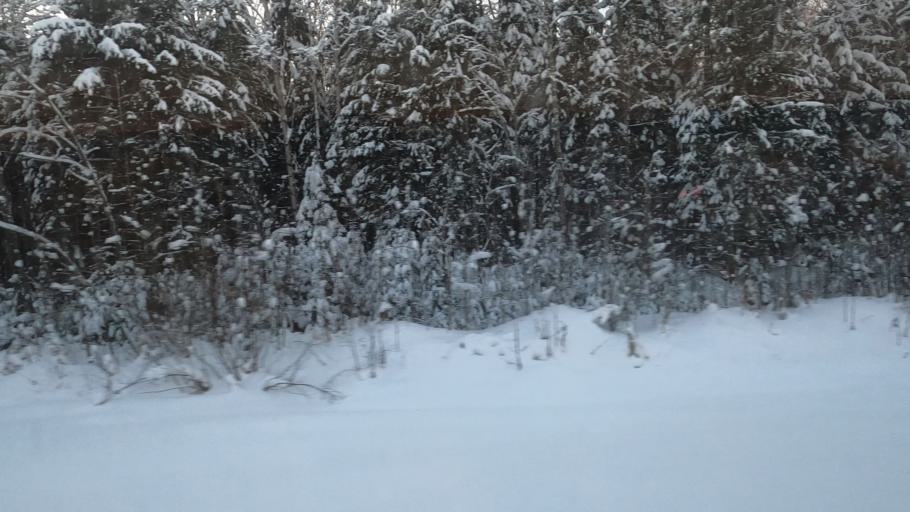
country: RU
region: Moskovskaya
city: Novo-Nikol'skoye
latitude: 56.6188
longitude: 37.5659
